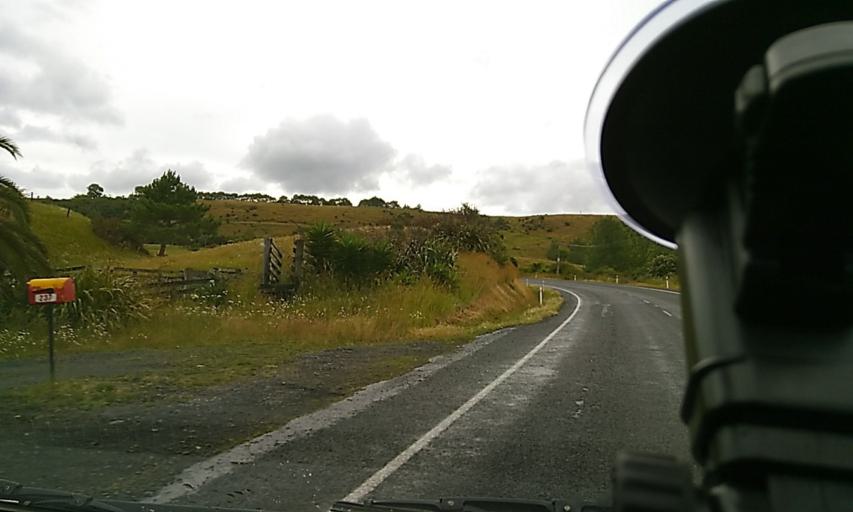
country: NZ
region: Auckland
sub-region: Auckland
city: Pukekohe East
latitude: -37.3185
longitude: 174.9562
